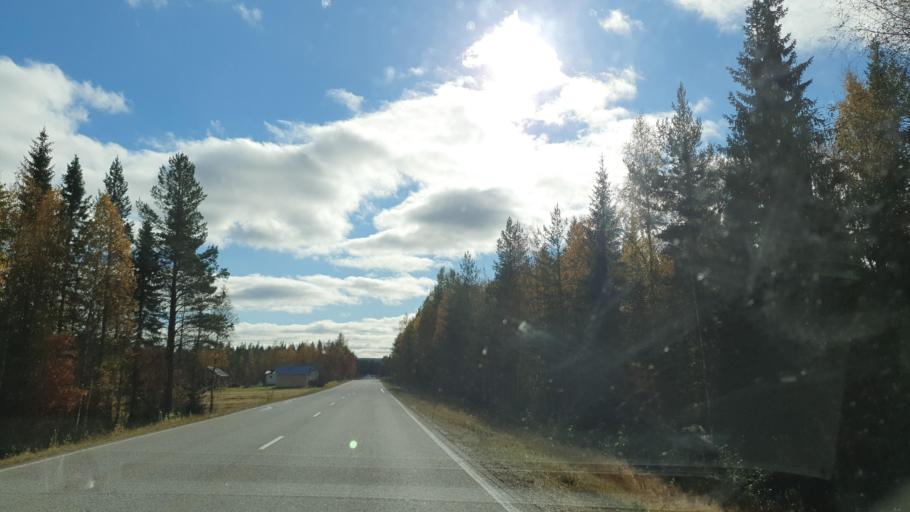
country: FI
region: Kainuu
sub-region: Kehys-Kainuu
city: Puolanka
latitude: 65.1952
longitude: 27.6172
